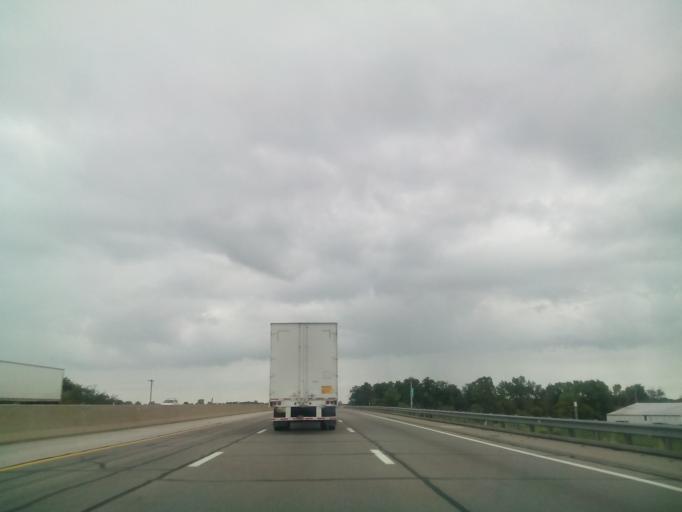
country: US
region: Ohio
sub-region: Sandusky County
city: Clyde
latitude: 41.3811
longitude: -83.0147
